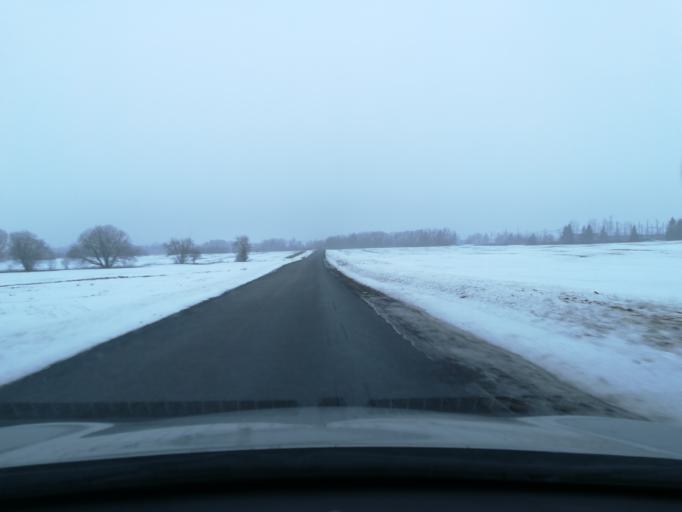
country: EE
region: Harju
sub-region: Raasiku vald
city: Raasiku
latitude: 59.3603
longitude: 25.1954
